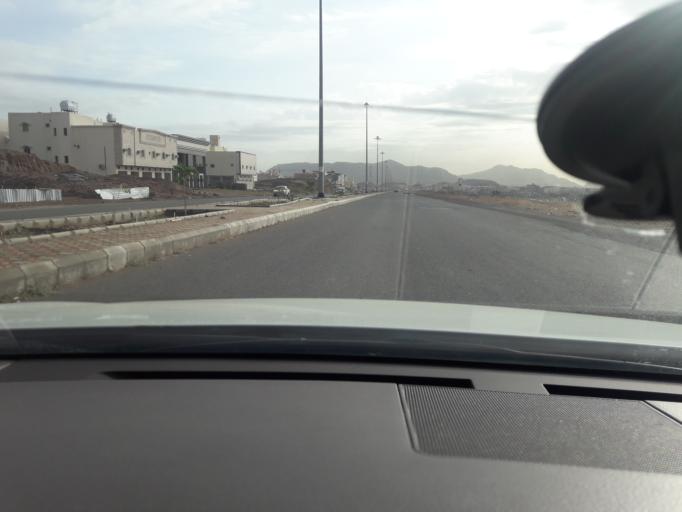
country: SA
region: Al Madinah al Munawwarah
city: Sultanah
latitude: 24.4665
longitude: 39.4779
